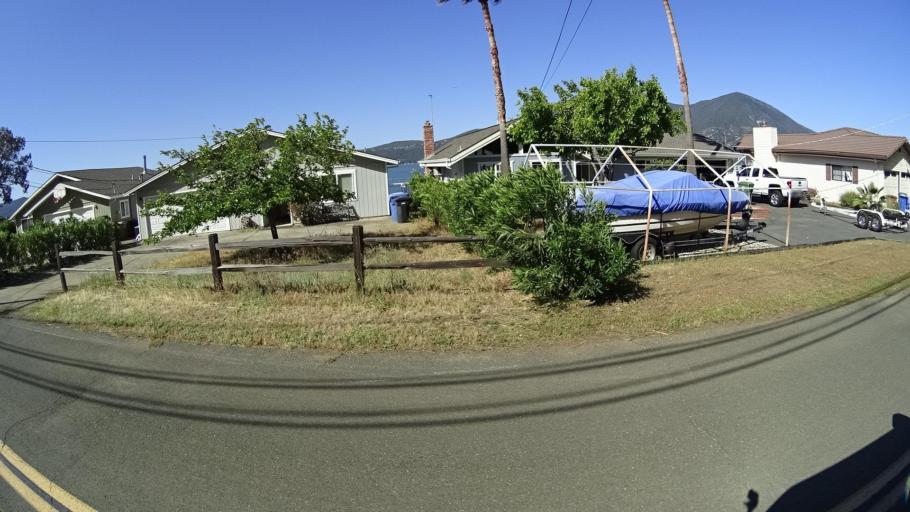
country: US
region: California
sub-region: Lake County
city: Clearlake Oaks
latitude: 38.9926
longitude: -122.7043
